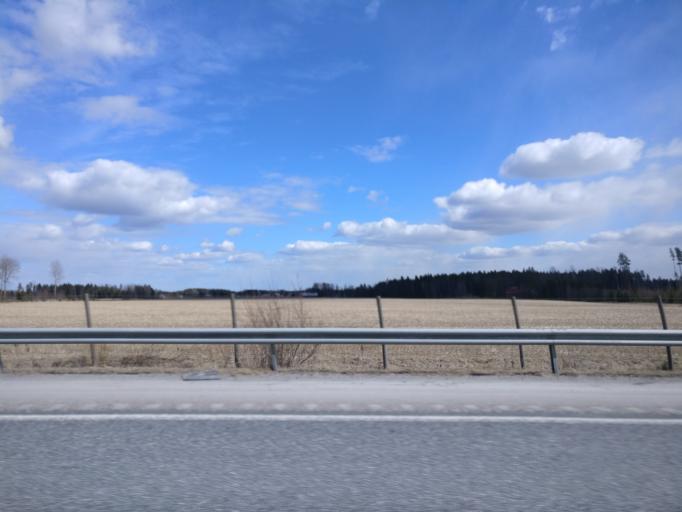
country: FI
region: Haeme
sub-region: Riihimaeki
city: Riihimaeki
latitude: 60.7718
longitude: 24.7159
